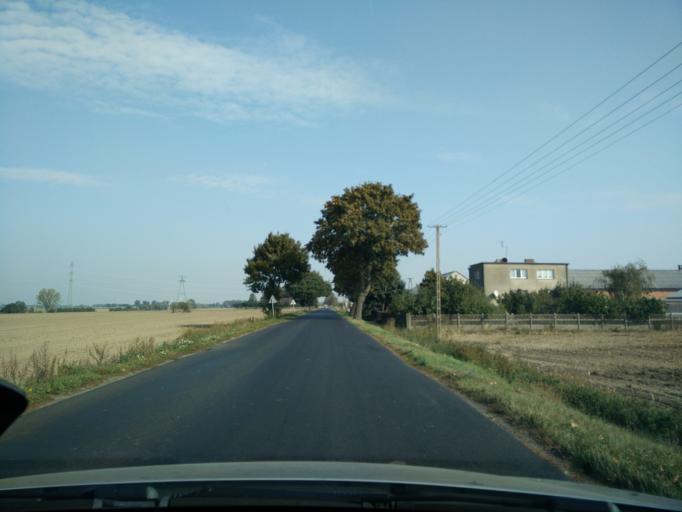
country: PL
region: Greater Poland Voivodeship
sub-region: Powiat sredzki
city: Dominowo
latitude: 52.2915
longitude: 17.3328
